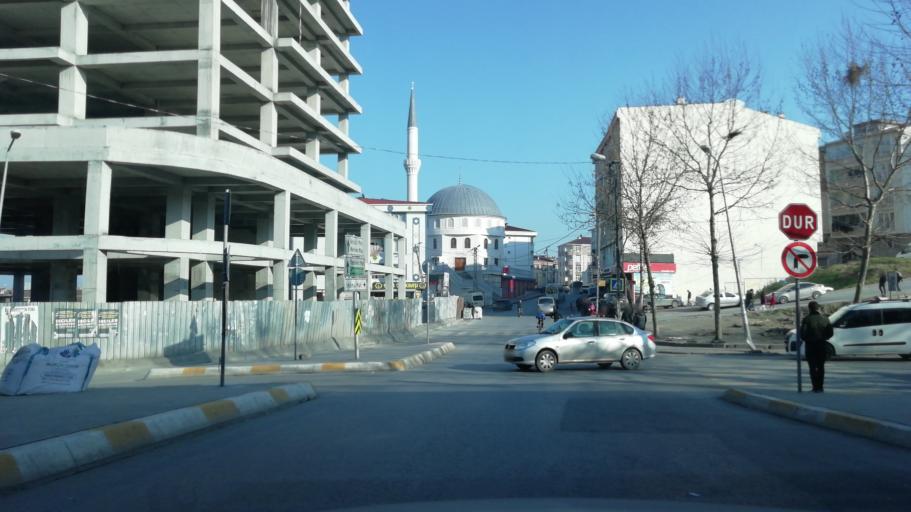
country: TR
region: Istanbul
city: Esenyurt
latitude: 41.0399
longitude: 28.6895
